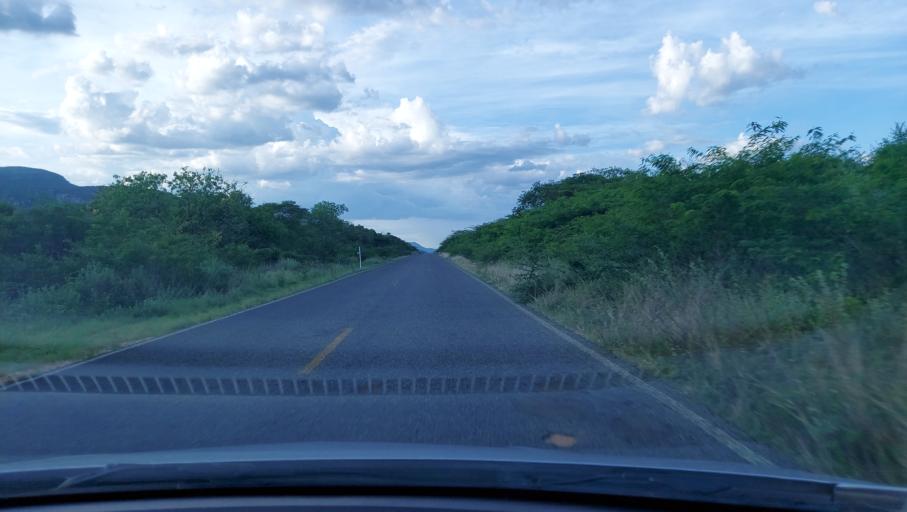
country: BR
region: Bahia
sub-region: Oliveira Dos Brejinhos
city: Beira Rio
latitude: -12.1827
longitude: -42.5411
